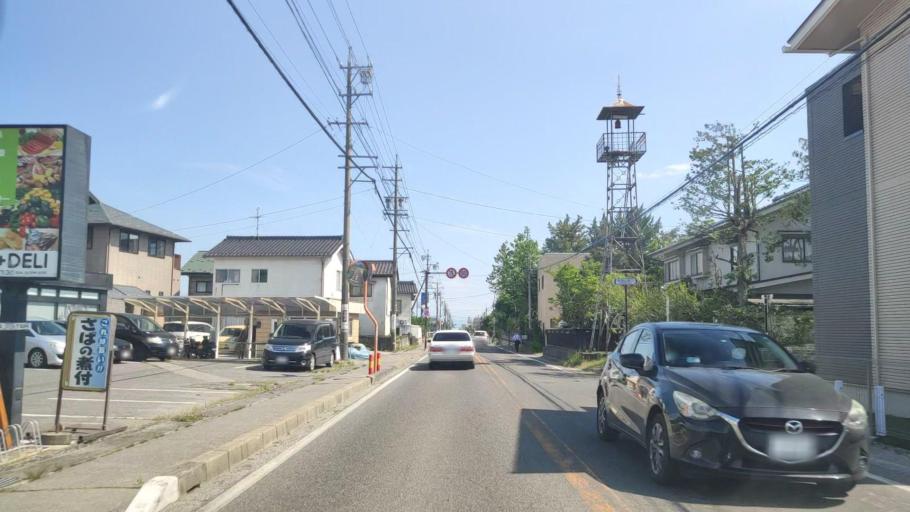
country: JP
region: Nagano
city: Hotaka
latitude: 36.3713
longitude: 137.8745
